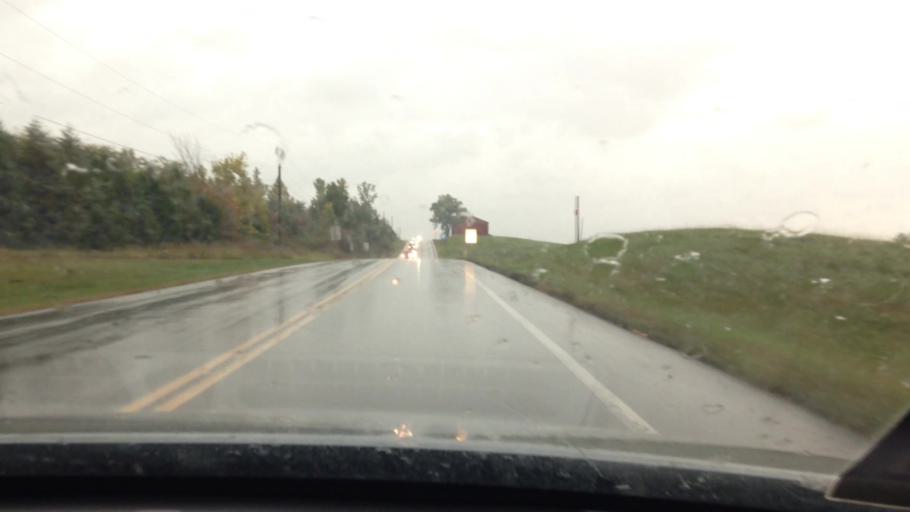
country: US
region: Missouri
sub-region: Platte County
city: Weston
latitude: 39.3930
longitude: -94.8634
